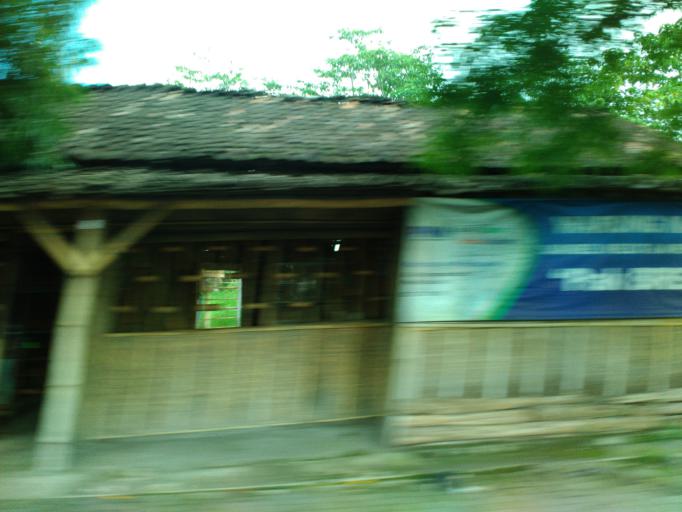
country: ID
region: Central Java
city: Delanggu
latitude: -7.6140
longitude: 110.7008
